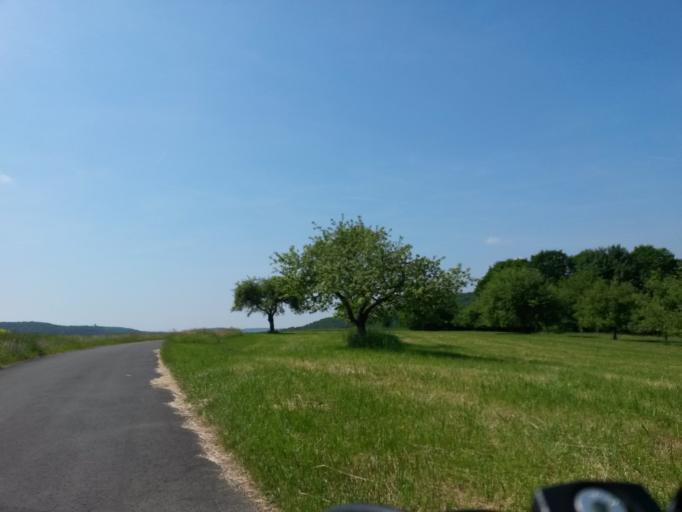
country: DE
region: Bavaria
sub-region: Regierungsbezirk Unterfranken
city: Euerdorf
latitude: 50.1592
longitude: 10.0008
